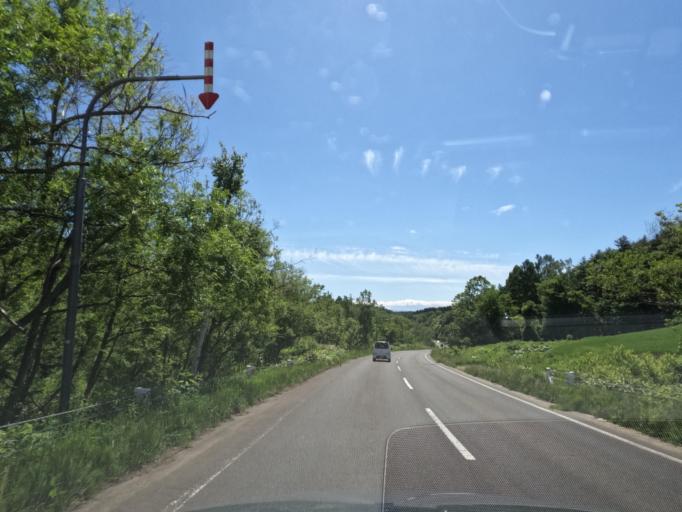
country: JP
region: Hokkaido
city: Iwamizawa
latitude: 43.1060
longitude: 141.7912
